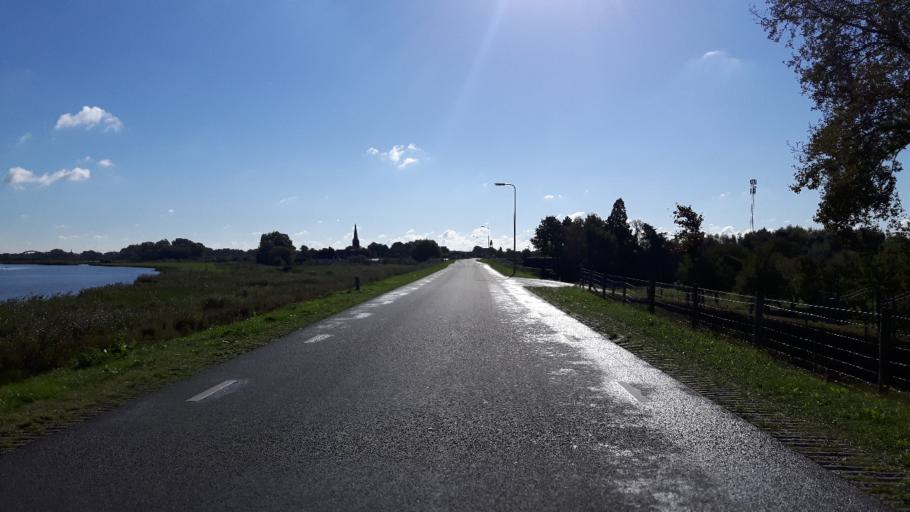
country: NL
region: Utrecht
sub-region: Gemeente Vianen
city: Vianen
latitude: 51.9694
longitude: 5.1489
